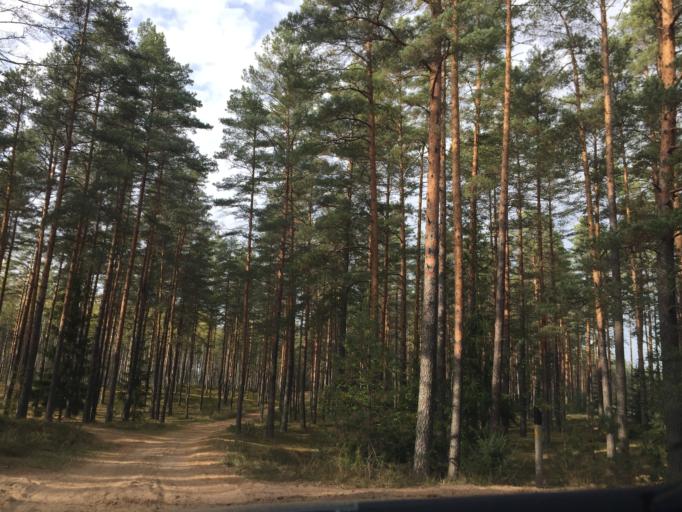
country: LV
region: Garkalne
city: Garkalne
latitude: 56.9513
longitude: 24.4272
